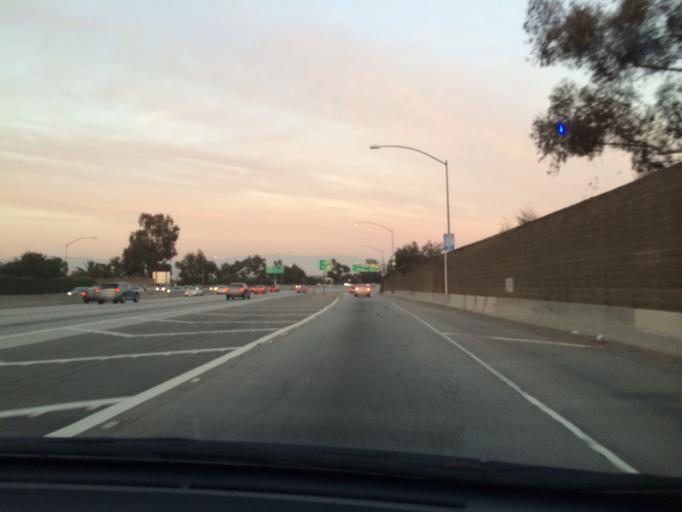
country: US
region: California
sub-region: Los Angeles County
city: Culver City
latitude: 34.0350
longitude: -118.3836
